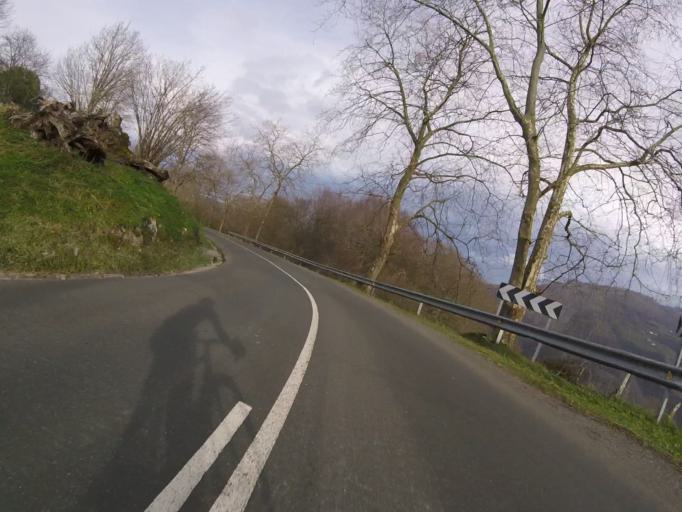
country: ES
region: Basque Country
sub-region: Provincia de Guipuzcoa
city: Beizama
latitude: 43.1628
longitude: -2.2068
